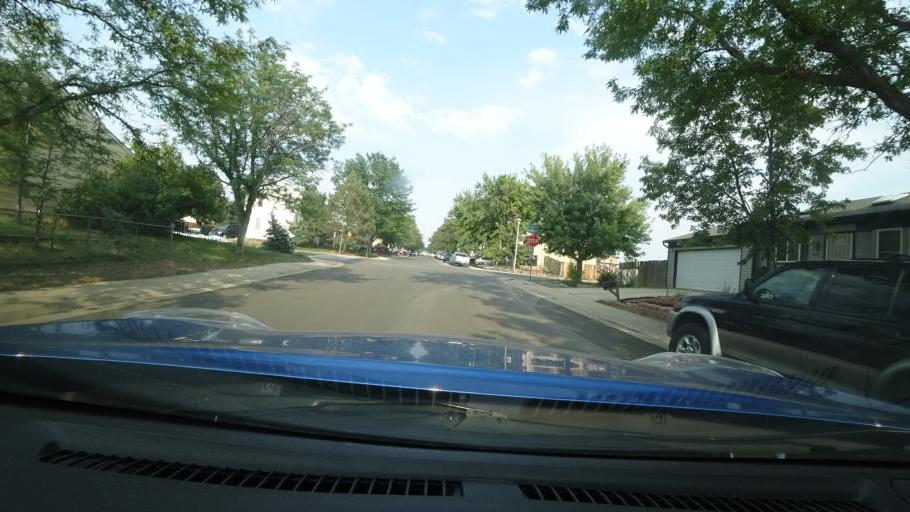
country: US
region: Colorado
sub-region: Adams County
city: Aurora
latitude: 39.7422
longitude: -104.7528
